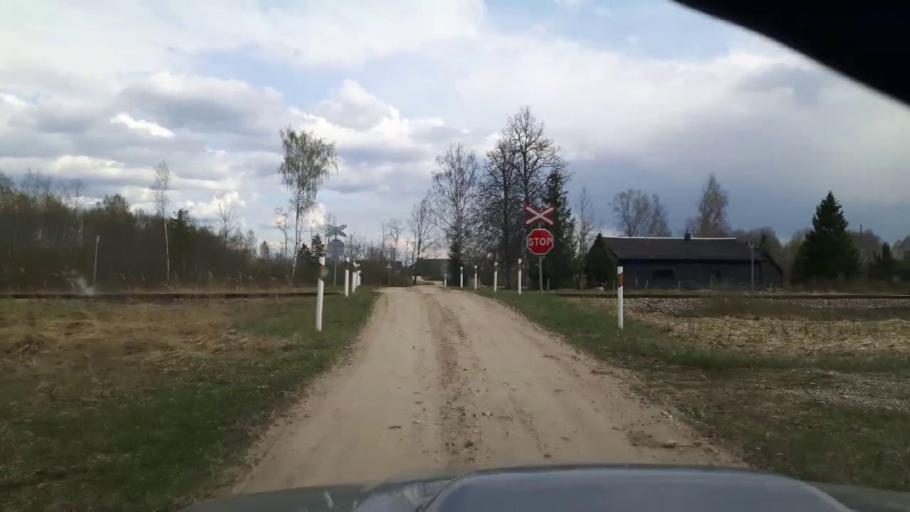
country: EE
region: Paernumaa
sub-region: Tootsi vald
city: Tootsi
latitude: 58.5074
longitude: 24.7923
